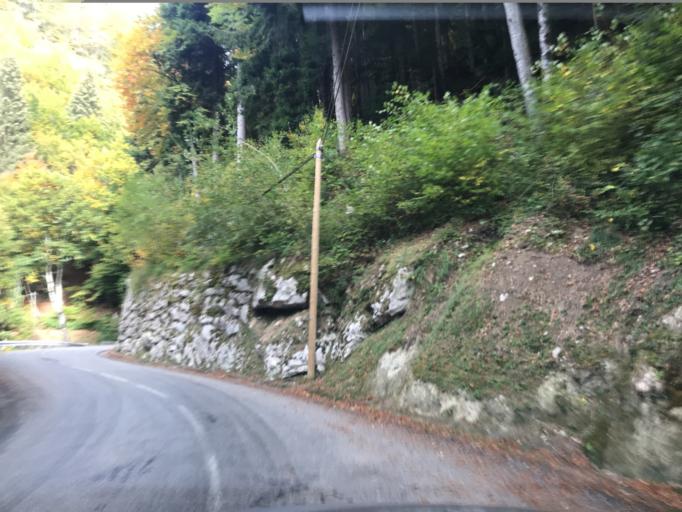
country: FR
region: Rhone-Alpes
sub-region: Departement de la Savoie
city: Les Echelles
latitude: 45.4343
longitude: 5.8164
